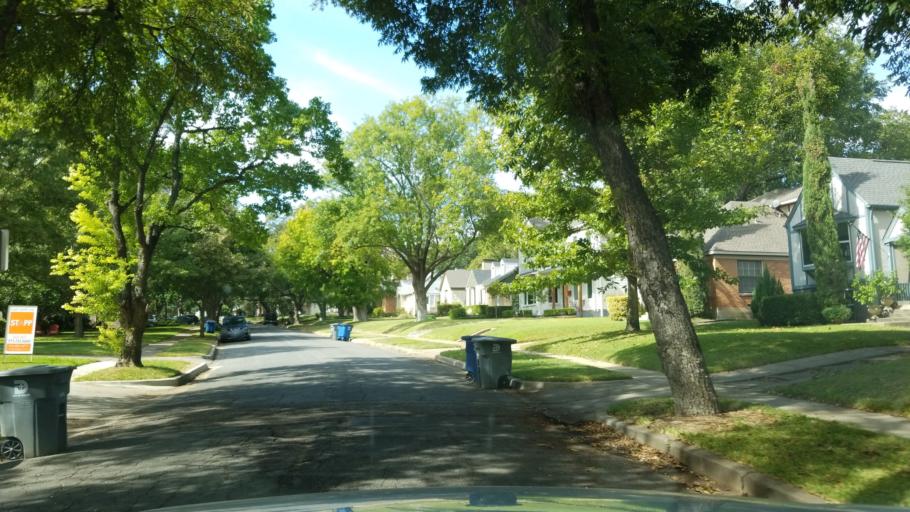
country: US
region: Texas
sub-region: Dallas County
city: Highland Park
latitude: 32.8116
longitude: -96.7339
